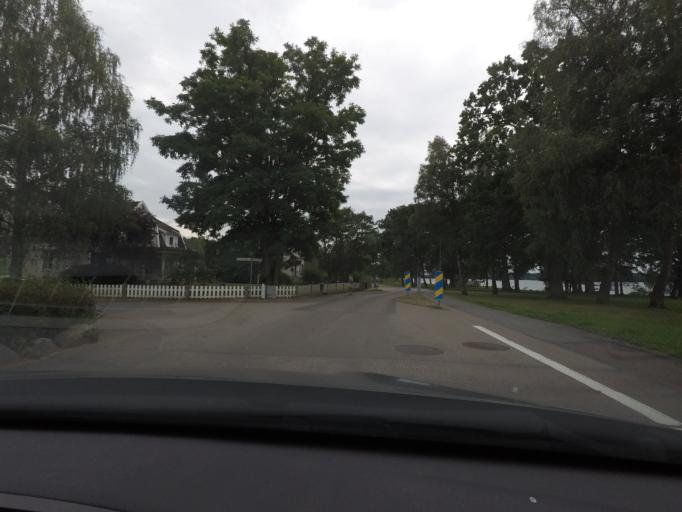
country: SE
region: Skane
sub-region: Osby Kommun
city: Osby
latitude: 56.3759
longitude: 14.0038
